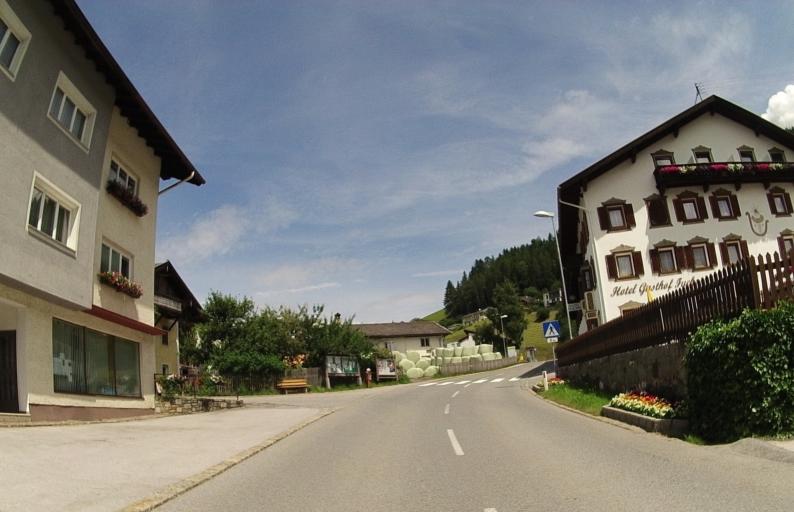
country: AT
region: Tyrol
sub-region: Politischer Bezirk Innsbruck Land
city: Pfons
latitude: 47.1414
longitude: 11.4603
